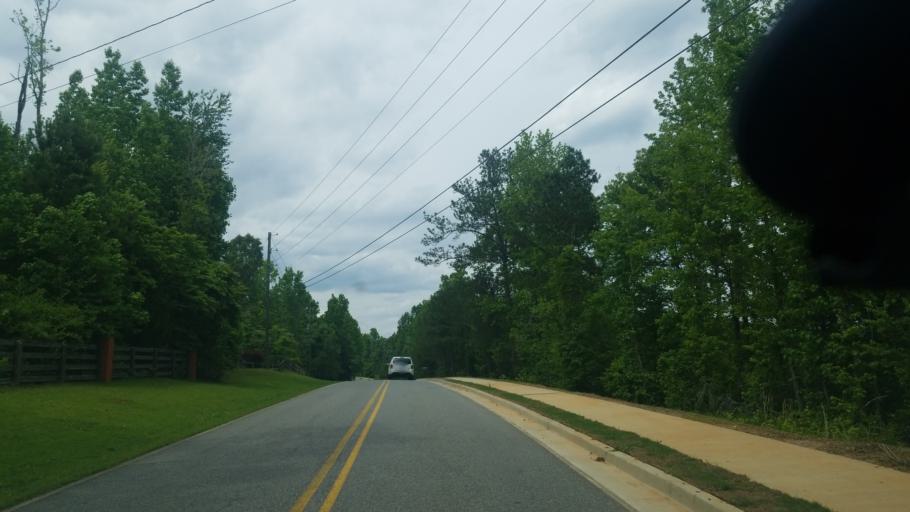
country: US
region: Georgia
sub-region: Forsyth County
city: Cumming
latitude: 34.1512
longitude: -84.1027
